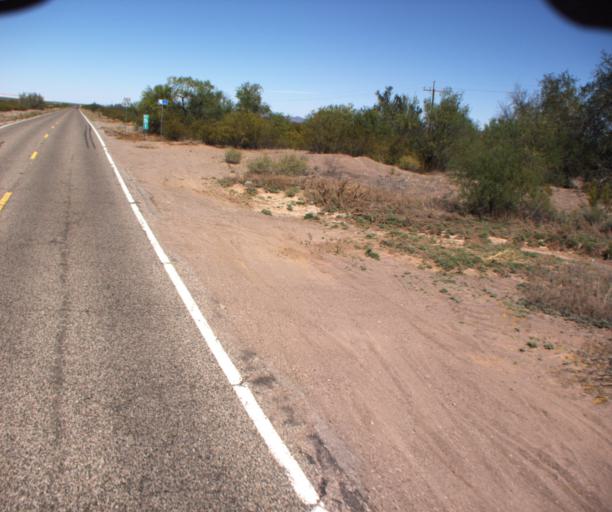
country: US
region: Arizona
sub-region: Pima County
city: Ajo
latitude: 32.2936
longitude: -112.7517
